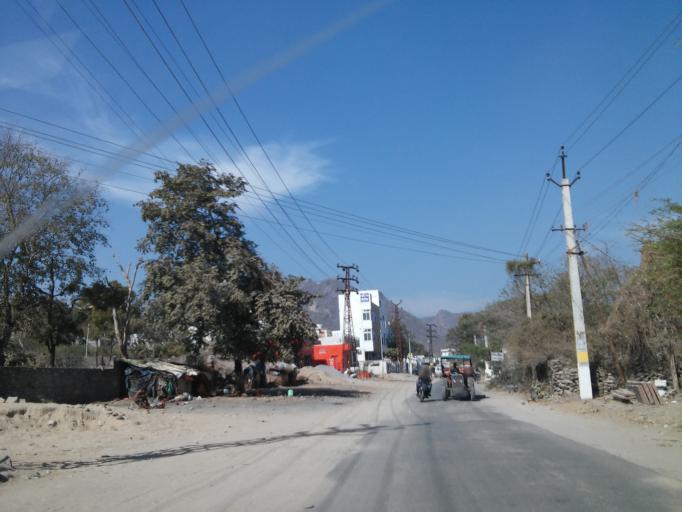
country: IN
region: Rajasthan
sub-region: Udaipur
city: Udaipur
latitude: 24.5810
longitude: 73.6529
